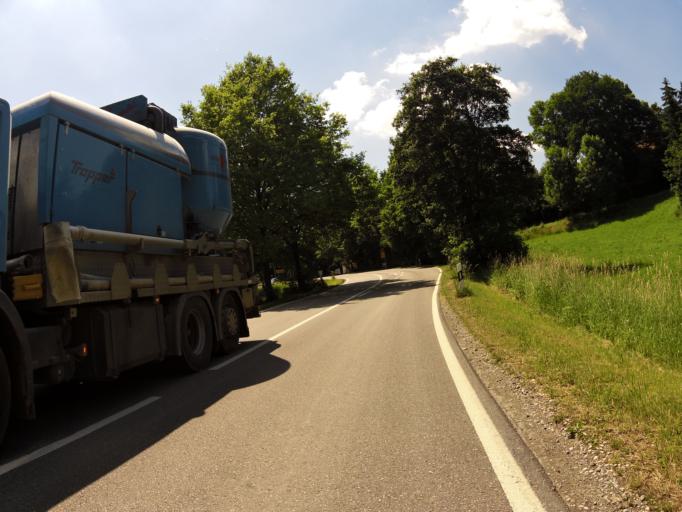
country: DE
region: Bavaria
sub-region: Upper Bavaria
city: Wang
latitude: 48.5019
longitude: 11.9566
